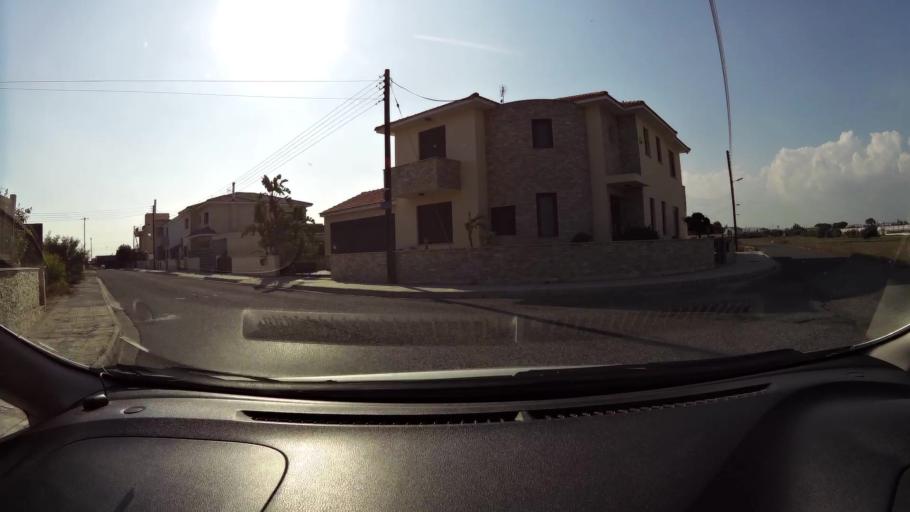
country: CY
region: Larnaka
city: Dhromolaxia
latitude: 34.8711
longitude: 33.5937
